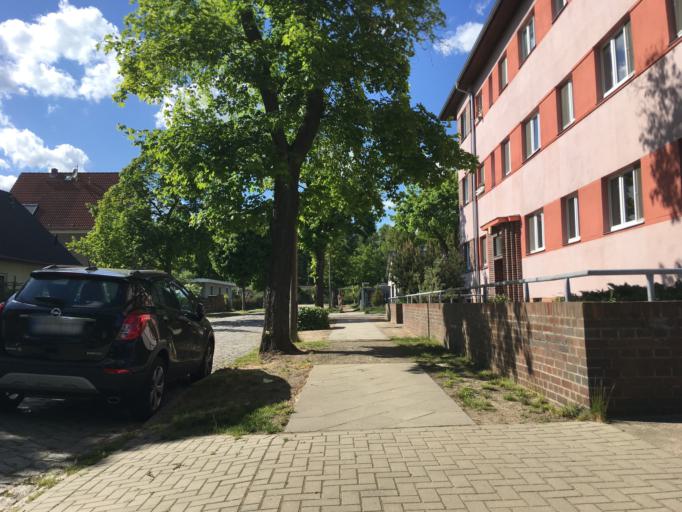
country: DE
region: Berlin
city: Buch
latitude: 52.6464
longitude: 13.5126
